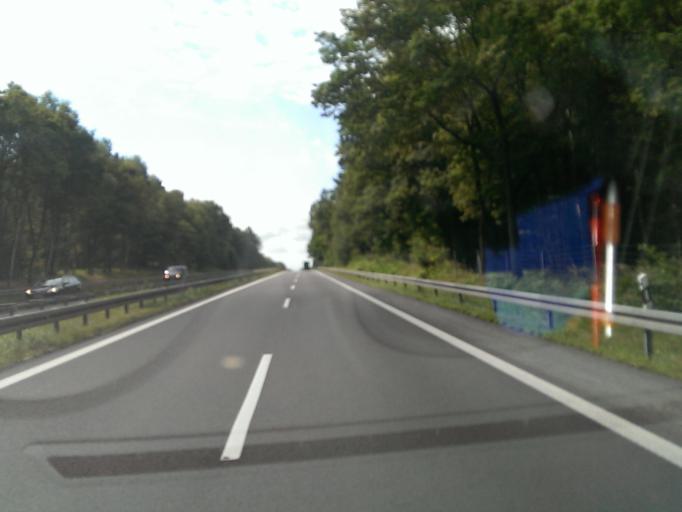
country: DE
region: Brandenburg
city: Bronkow
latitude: 51.6885
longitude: 13.9011
